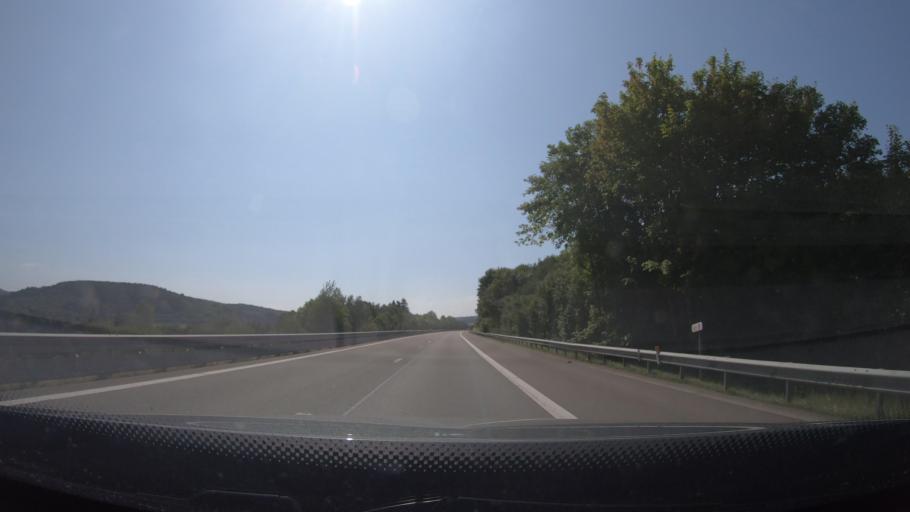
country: BE
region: Wallonia
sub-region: Province de Liege
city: Malmedy
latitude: 50.3803
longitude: 6.0041
